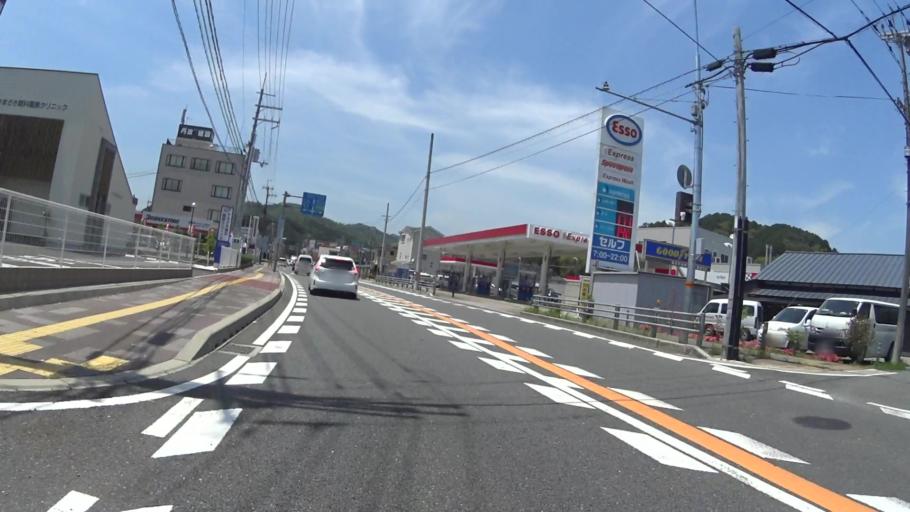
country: JP
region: Kyoto
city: Kameoka
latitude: 35.1115
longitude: 135.4691
